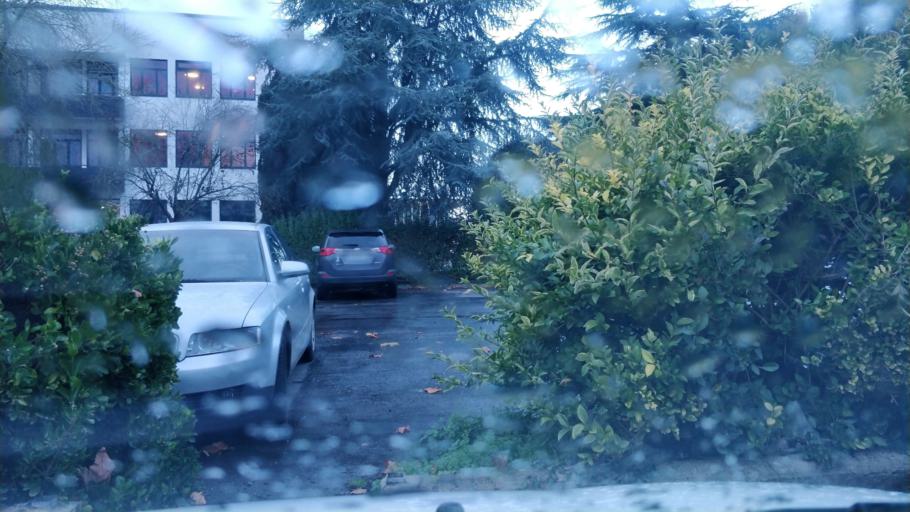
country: FR
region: Brittany
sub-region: Departement du Morbihan
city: Pontivy
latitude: 48.0711
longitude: -2.9645
